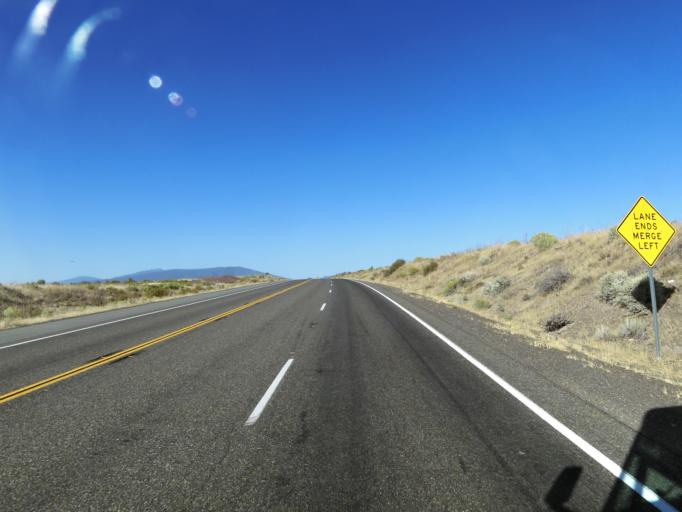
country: US
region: California
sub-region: Siskiyou County
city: Weed
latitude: 41.4808
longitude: -122.3445
